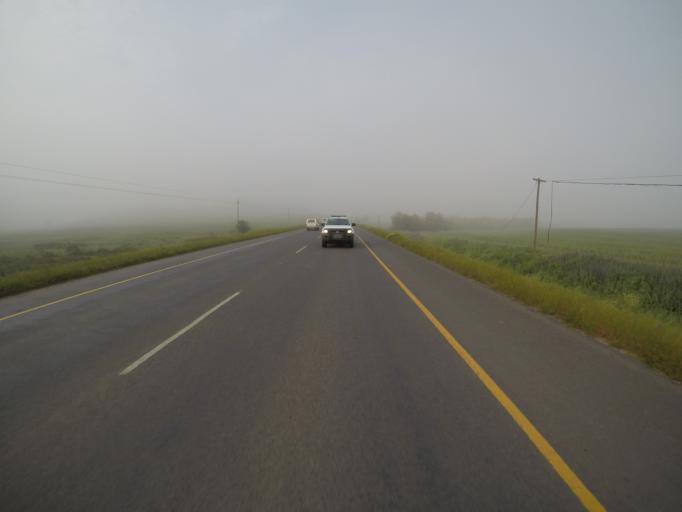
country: ZA
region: Western Cape
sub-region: City of Cape Town
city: Kraaifontein
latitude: -33.7755
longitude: 18.7081
